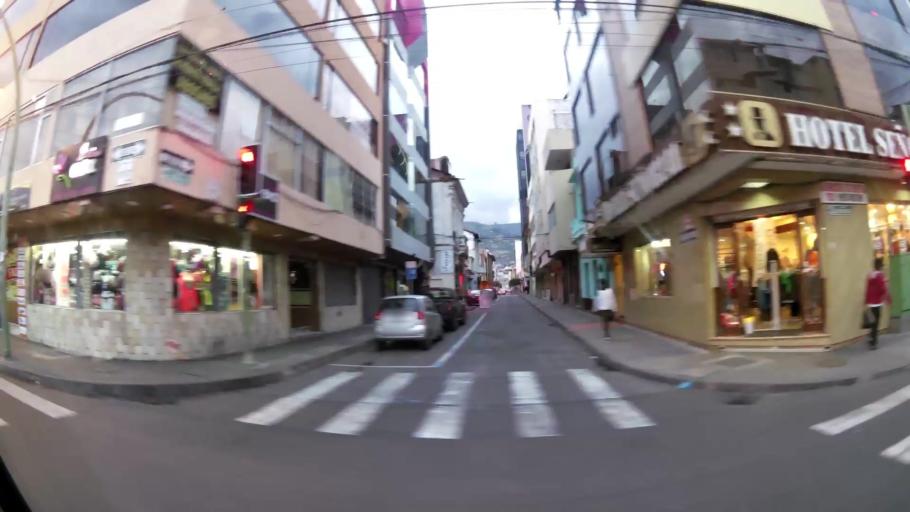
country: EC
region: Tungurahua
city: Ambato
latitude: -1.2440
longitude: -78.6294
